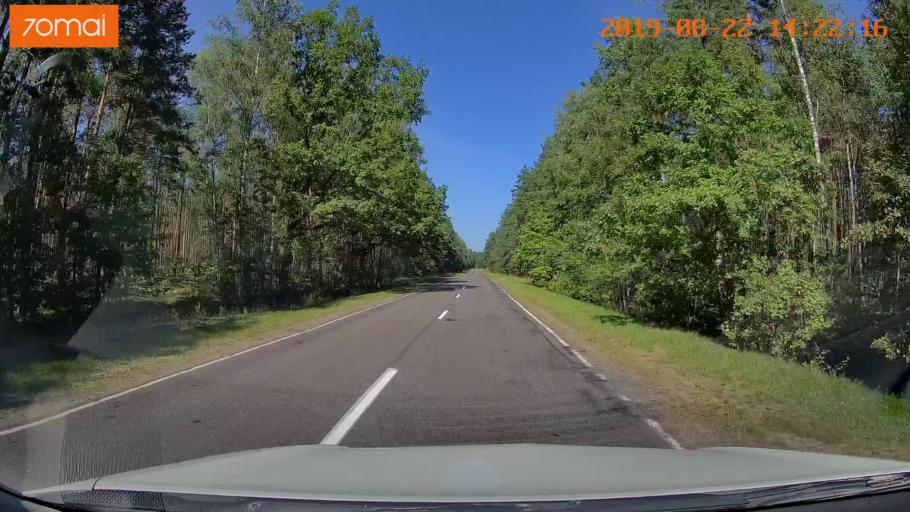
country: BY
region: Mogilev
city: Asipovichy
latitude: 53.2744
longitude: 28.5688
